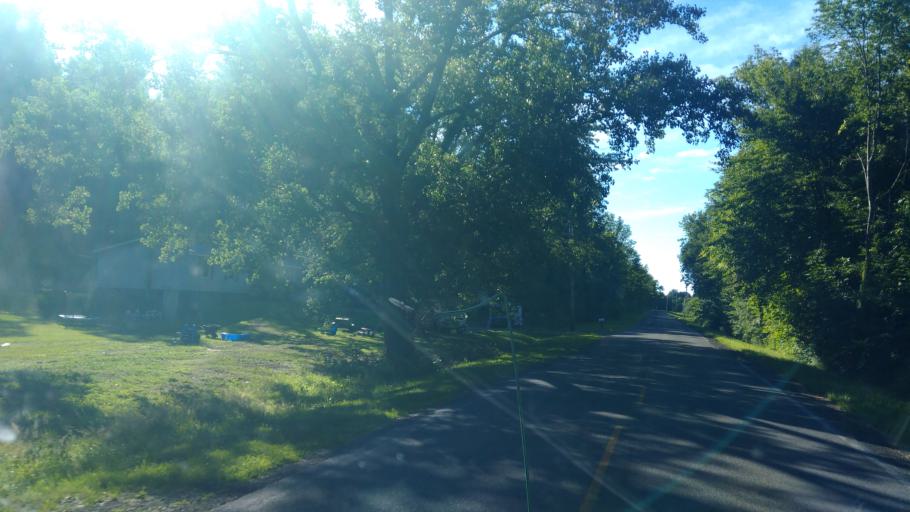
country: US
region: New York
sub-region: Wayne County
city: Lyons
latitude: 43.0067
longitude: -76.9726
